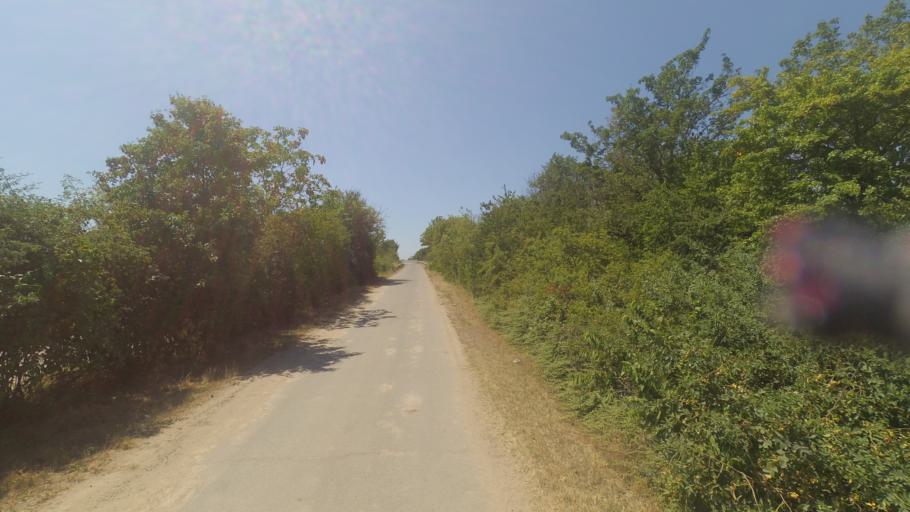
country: DE
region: Rheinland-Pfalz
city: Gartenstadt
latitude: 49.4407
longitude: 8.4082
